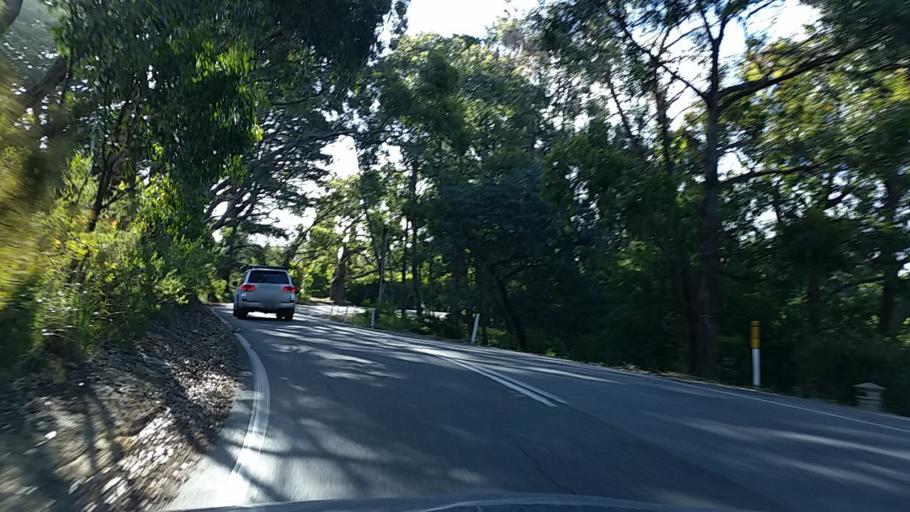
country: AU
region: South Australia
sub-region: Adelaide Hills
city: Stirling
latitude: -35.0200
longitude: 138.7521
